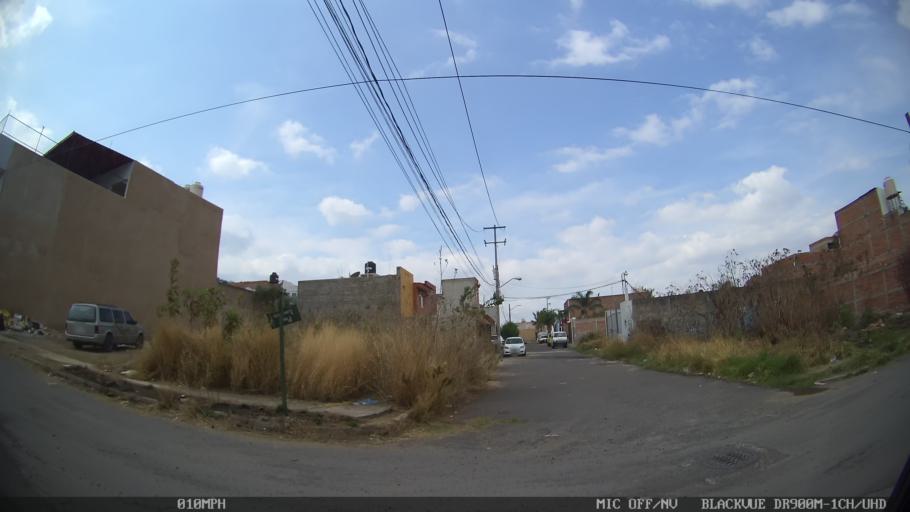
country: MX
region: Jalisco
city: Coyula
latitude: 20.6379
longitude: -103.2188
